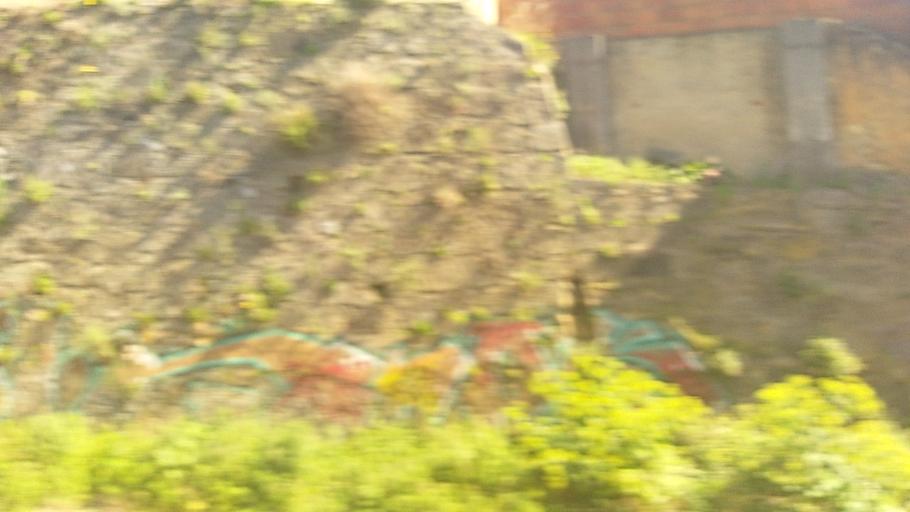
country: PT
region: Lisbon
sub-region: Lisbon
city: Lisbon
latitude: 38.7336
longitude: -9.1081
